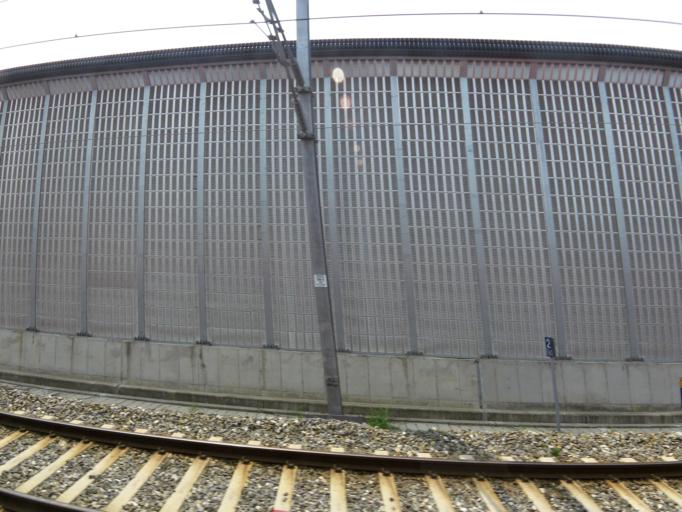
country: KR
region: Daejeon
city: Daejeon
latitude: 36.3203
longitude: 127.4411
